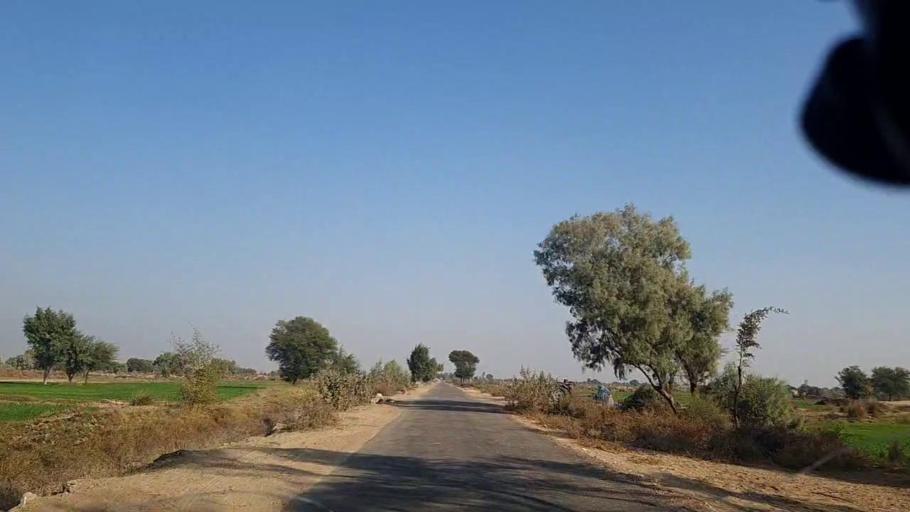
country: PK
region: Sindh
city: Khanpur
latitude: 27.6881
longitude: 69.5045
